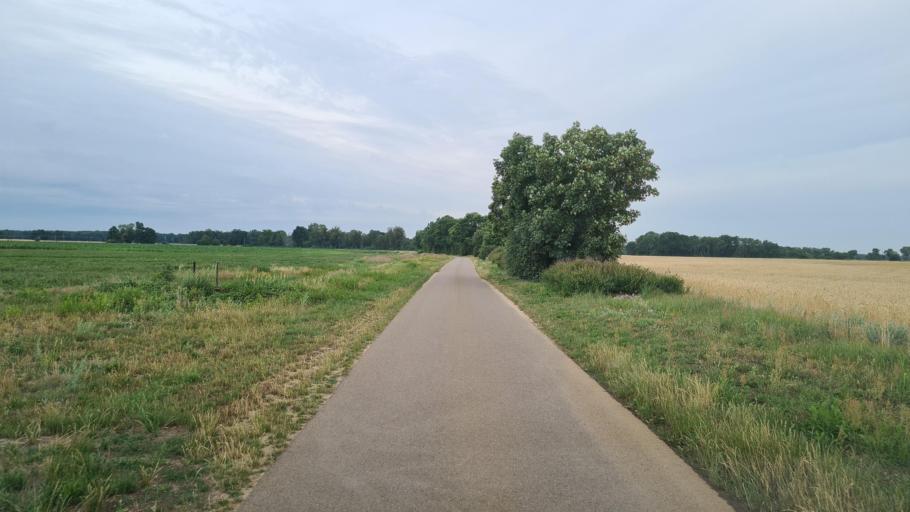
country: DE
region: Saxony-Anhalt
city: Annaburg
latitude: 51.7535
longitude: 13.0152
